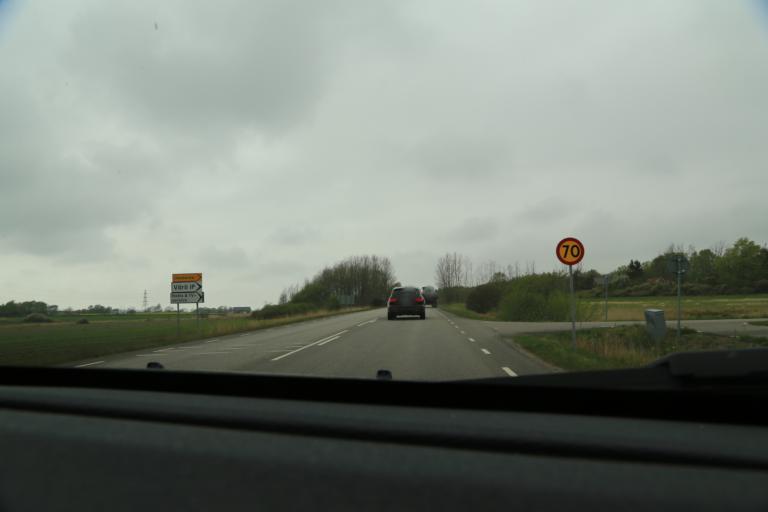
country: SE
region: Halland
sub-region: Kungsbacka Kommun
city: Frillesas
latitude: 57.2361
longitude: 12.1815
